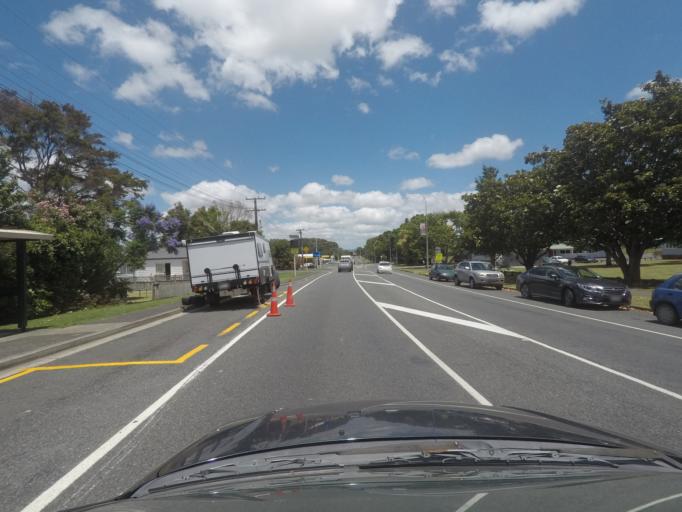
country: NZ
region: Northland
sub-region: Whangarei
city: Whangarei
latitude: -35.7561
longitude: 174.3685
